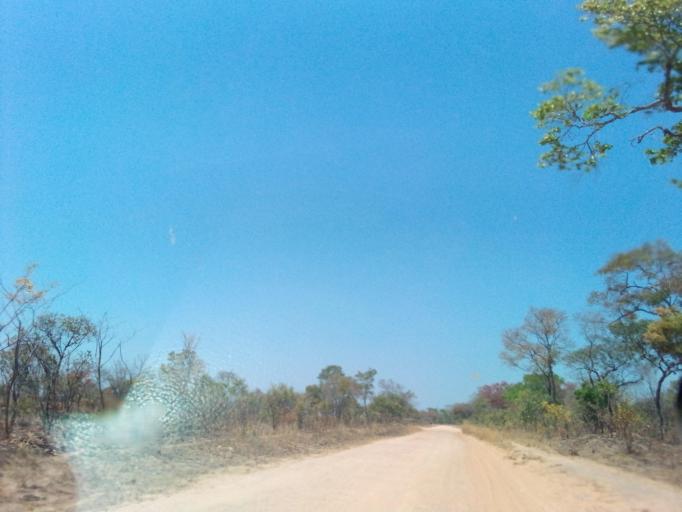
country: ZM
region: Northern
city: Mpika
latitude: -12.2305
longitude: 30.6571
